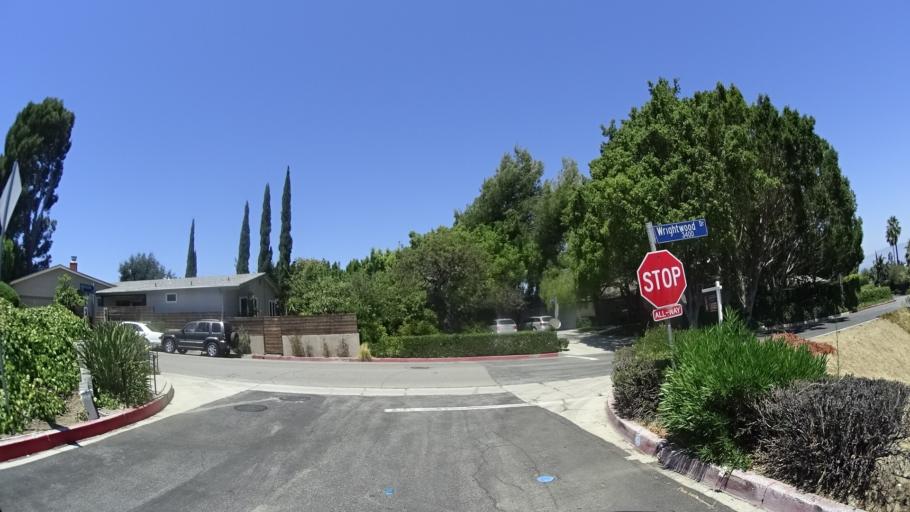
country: US
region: California
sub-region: Los Angeles County
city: Universal City
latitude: 34.1341
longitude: -118.3741
